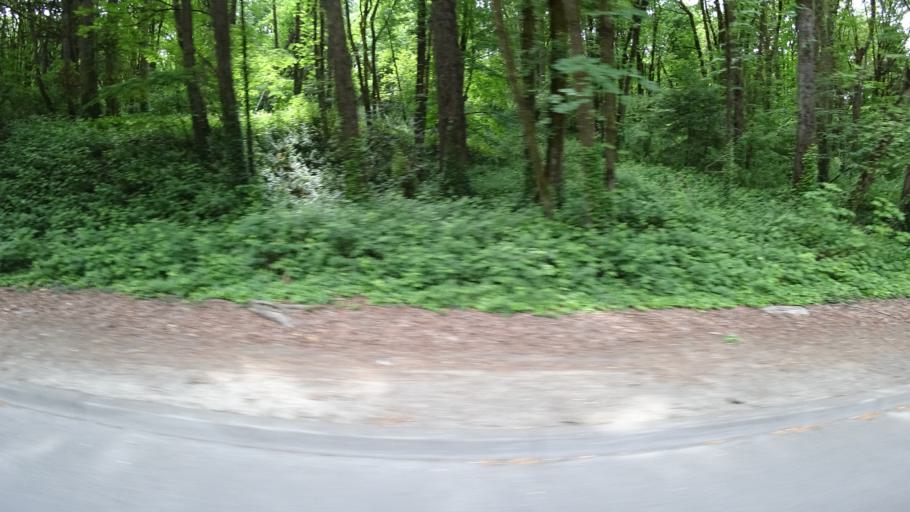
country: US
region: Oregon
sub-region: Multnomah County
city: Portland
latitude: 45.4832
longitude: -122.6807
